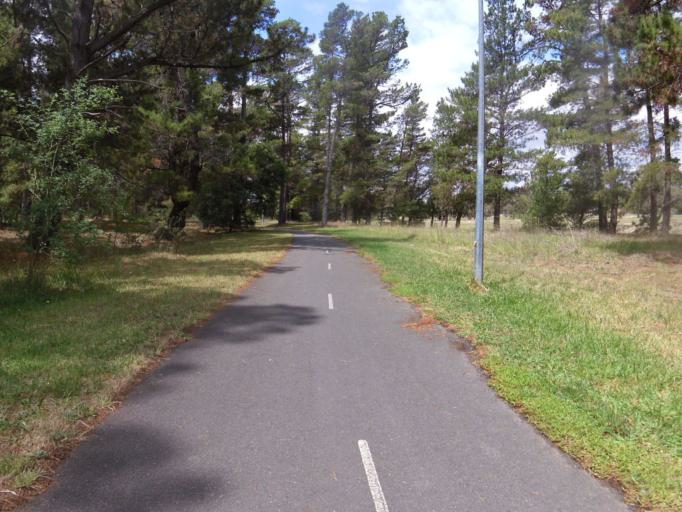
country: AU
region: Australian Capital Territory
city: Macarthur
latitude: -35.4145
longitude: 149.1153
